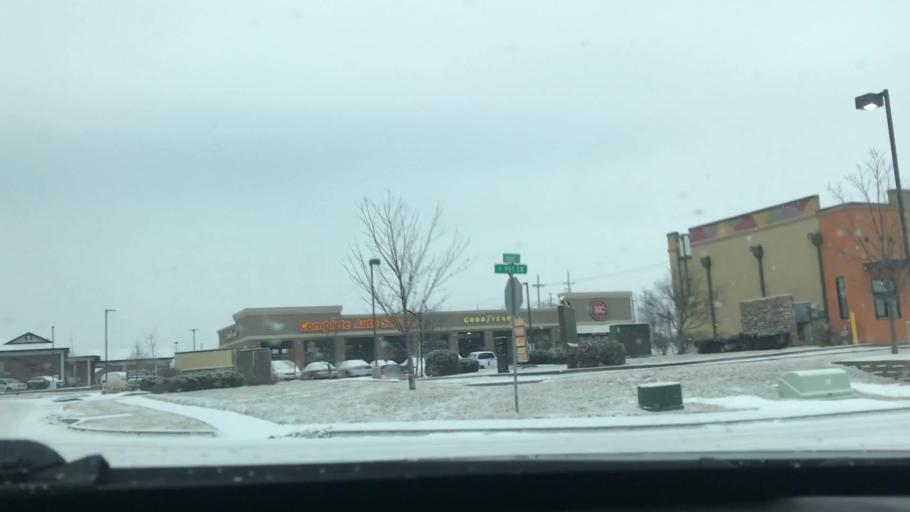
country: US
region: Missouri
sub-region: Clay County
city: Gladstone
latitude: 39.2660
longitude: -94.5768
